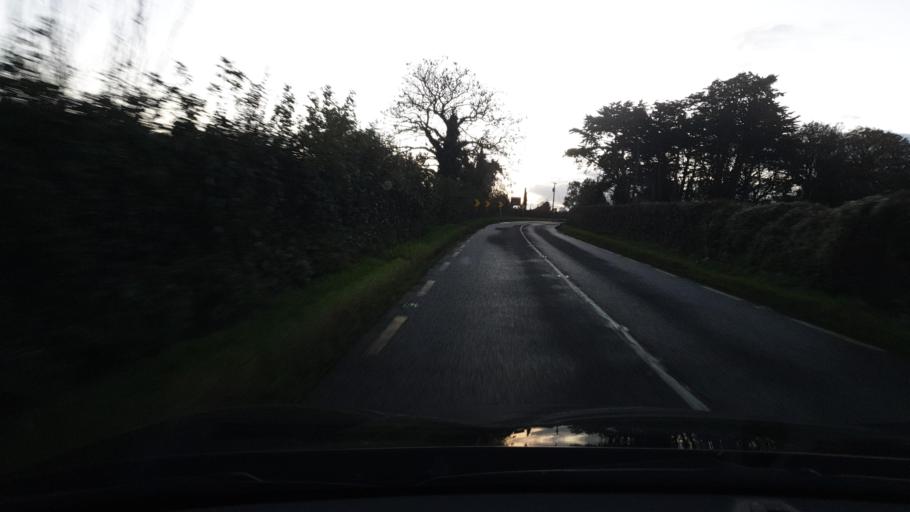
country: IE
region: Leinster
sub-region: An Mhi
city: Slane
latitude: 53.7106
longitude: -6.4973
